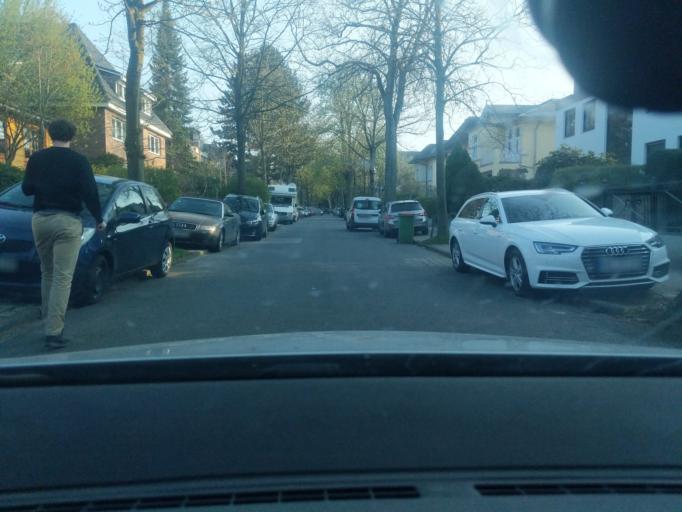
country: DE
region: Hamburg
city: Hamburg-Nord
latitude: 53.6010
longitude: 9.9681
